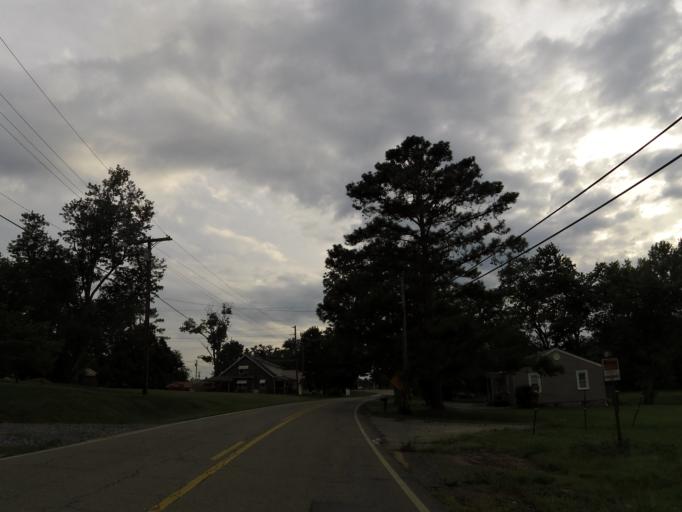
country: US
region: Tennessee
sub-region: Loudon County
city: Greenback
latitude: 35.6625
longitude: -84.1683
